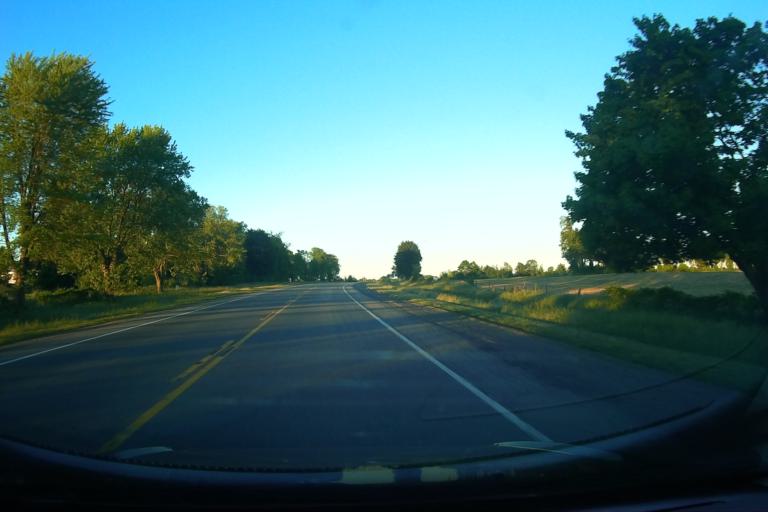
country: CA
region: Ontario
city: Casselman
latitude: 45.1032
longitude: -75.2481
